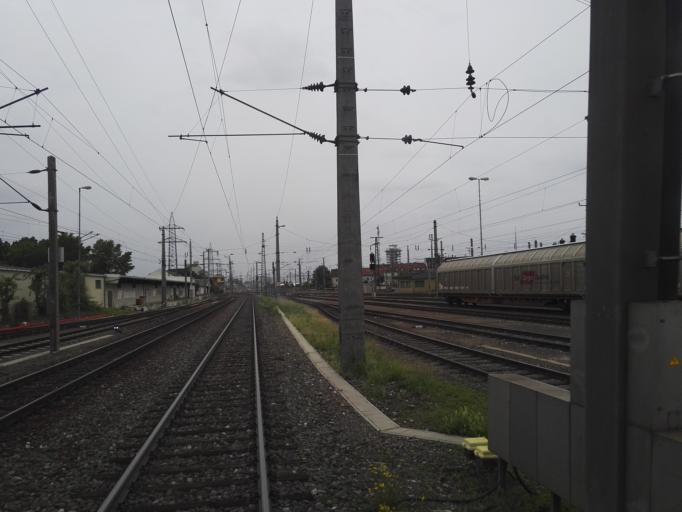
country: AT
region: Styria
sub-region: Graz Stadt
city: Goesting
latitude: 47.0859
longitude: 15.4094
